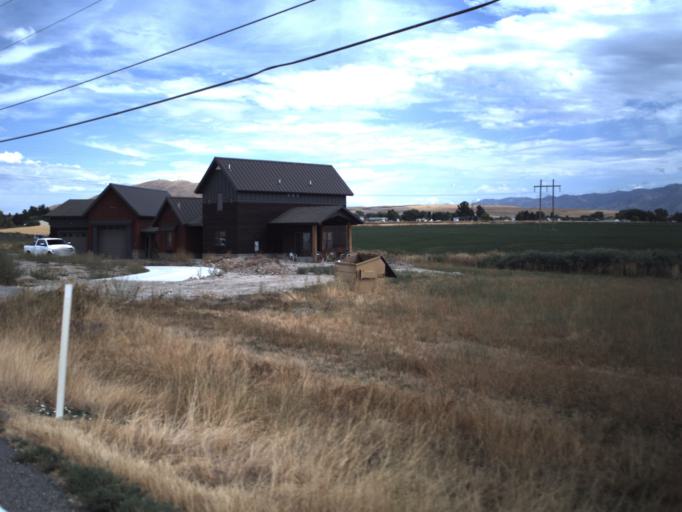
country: US
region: Utah
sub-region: Cache County
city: Benson
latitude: 41.8507
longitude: -112.0015
